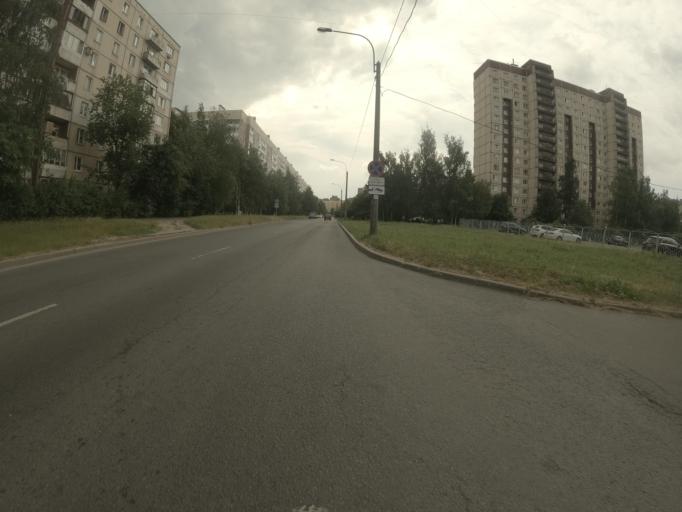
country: RU
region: St.-Petersburg
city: Krasnogvargeisky
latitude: 59.9286
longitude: 30.4763
